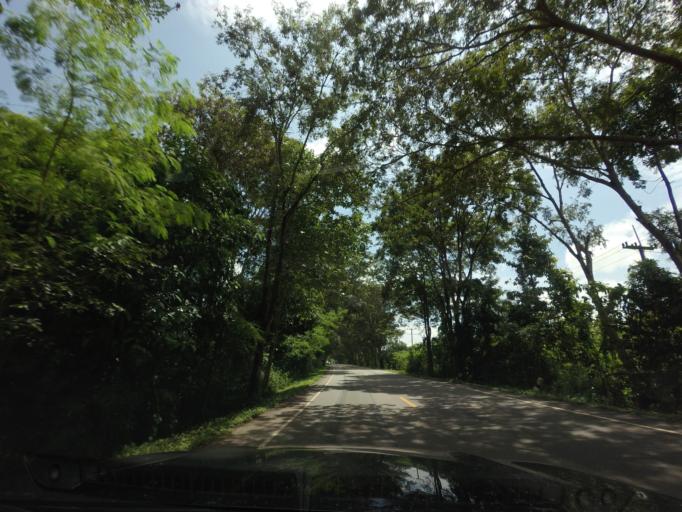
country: TH
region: Nong Khai
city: Pho Tak
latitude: 17.7896
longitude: 102.3613
